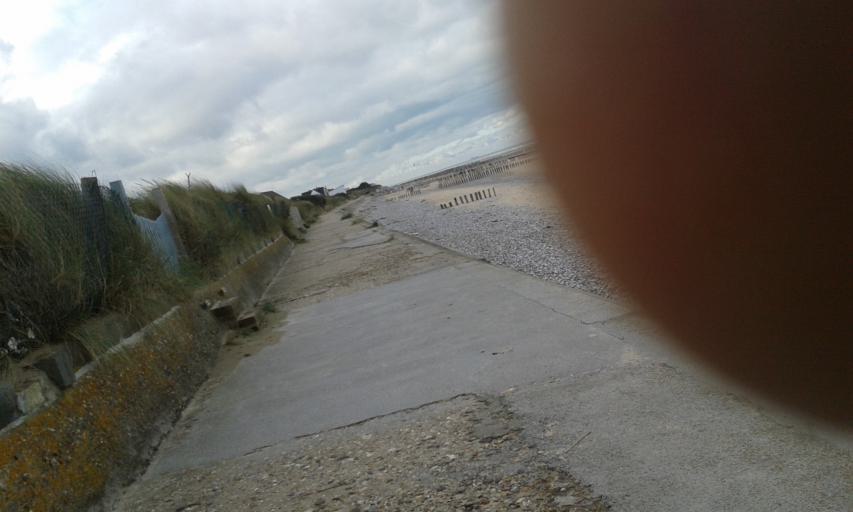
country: FR
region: Nord-Pas-de-Calais
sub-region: Departement du Pas-de-Calais
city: Sangatte
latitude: 50.9489
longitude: 1.7615
